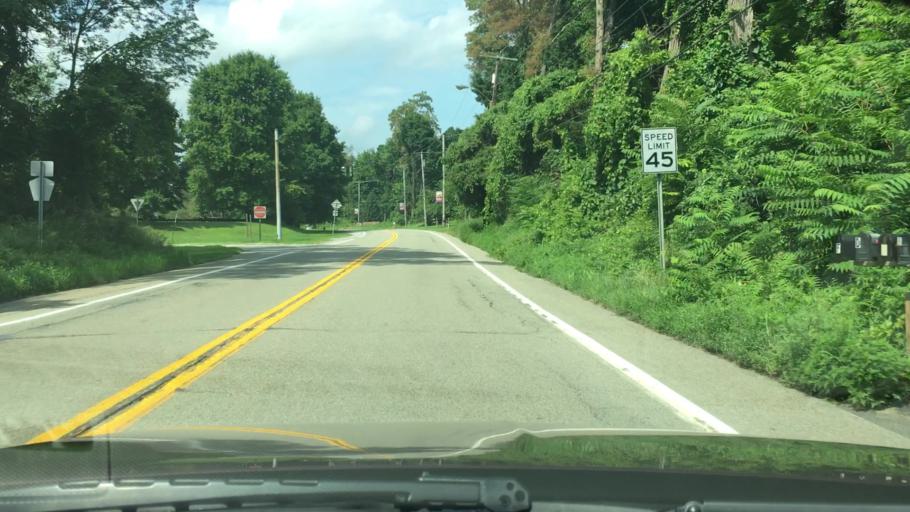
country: US
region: New York
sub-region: Dutchess County
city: Brinckerhoff
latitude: 41.5466
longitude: -73.8216
